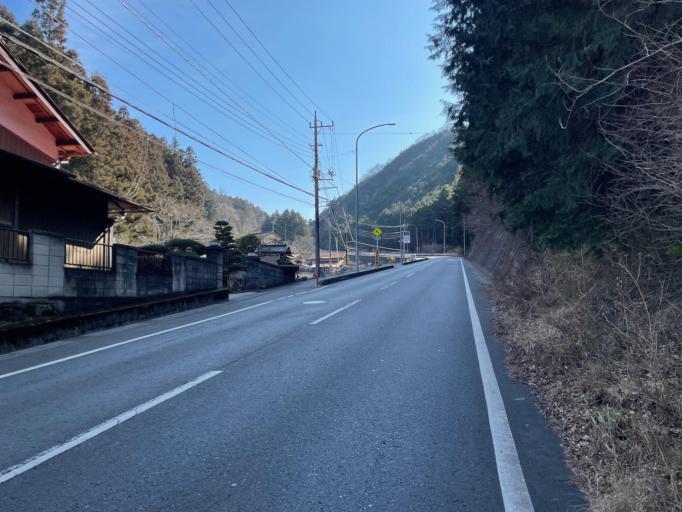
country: JP
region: Tokyo
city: Ome
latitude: 35.8602
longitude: 139.2389
